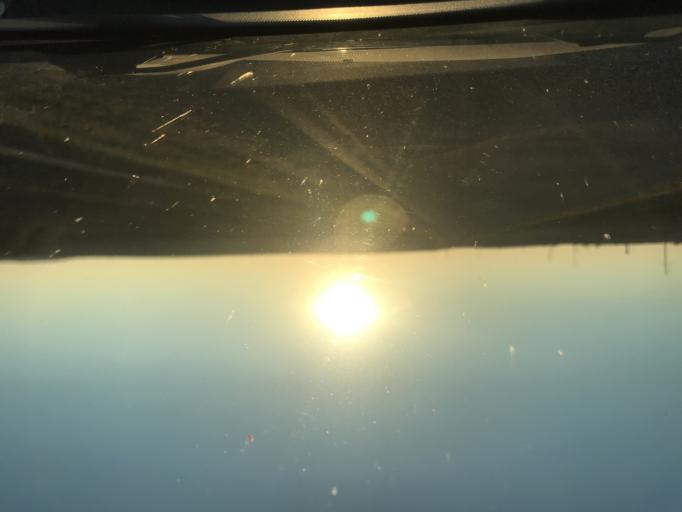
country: BY
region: Gomel
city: Brahin
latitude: 51.8417
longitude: 30.3408
